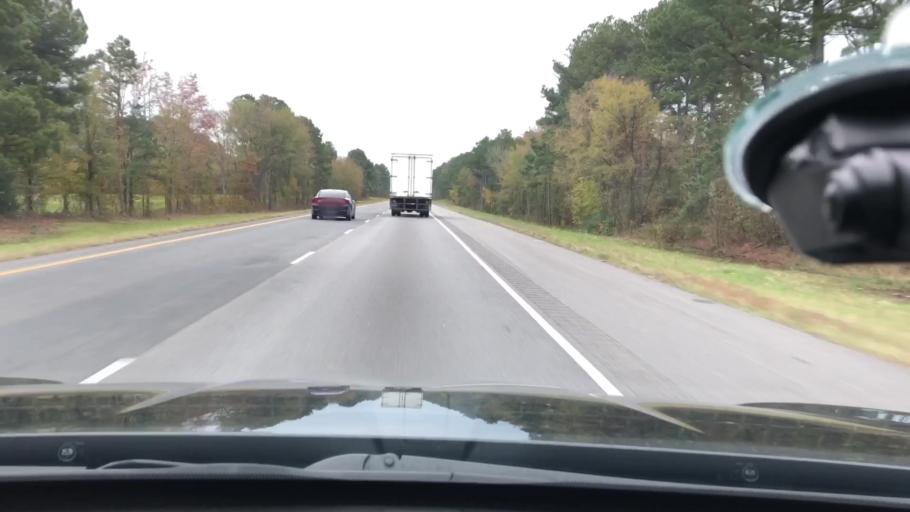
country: US
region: Arkansas
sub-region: Hempstead County
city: Hope
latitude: 33.6266
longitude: -93.7472
